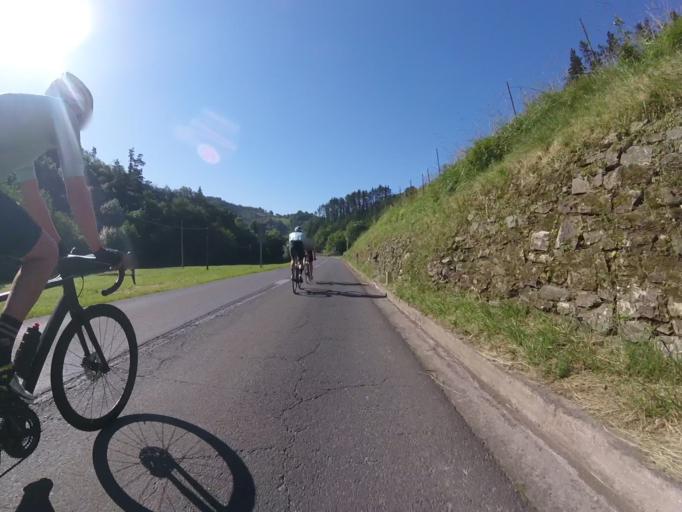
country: ES
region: Basque Country
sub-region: Provincia de Guipuzcoa
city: Beizama
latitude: 43.1499
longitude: -2.2375
